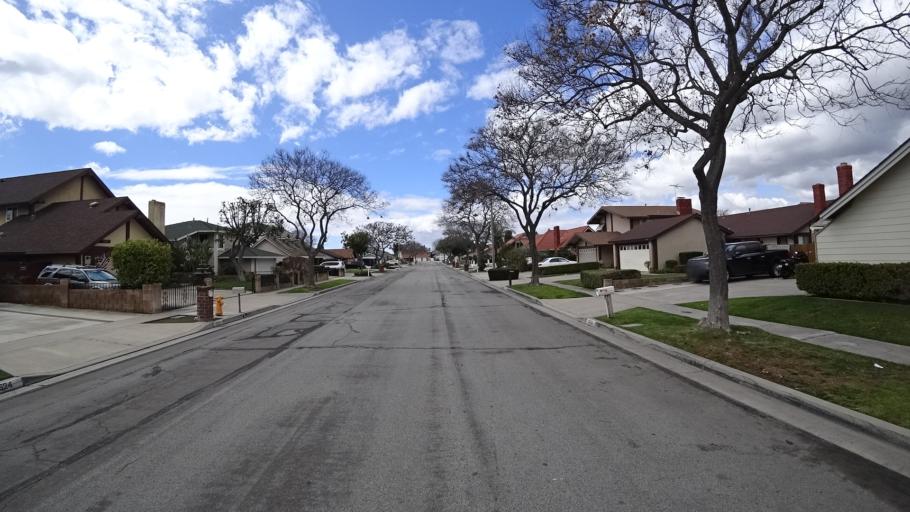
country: US
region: California
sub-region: Orange County
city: Anaheim
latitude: 33.8268
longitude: -117.9340
